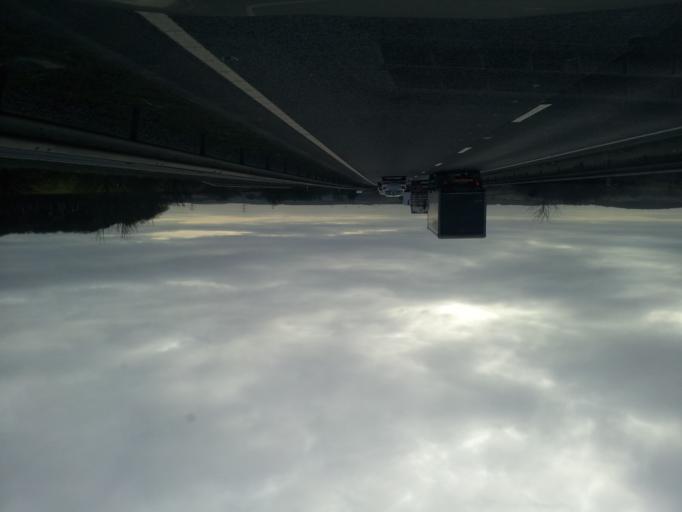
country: GB
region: England
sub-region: Lincolnshire
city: Grantham
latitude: 52.8883
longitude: -0.6444
